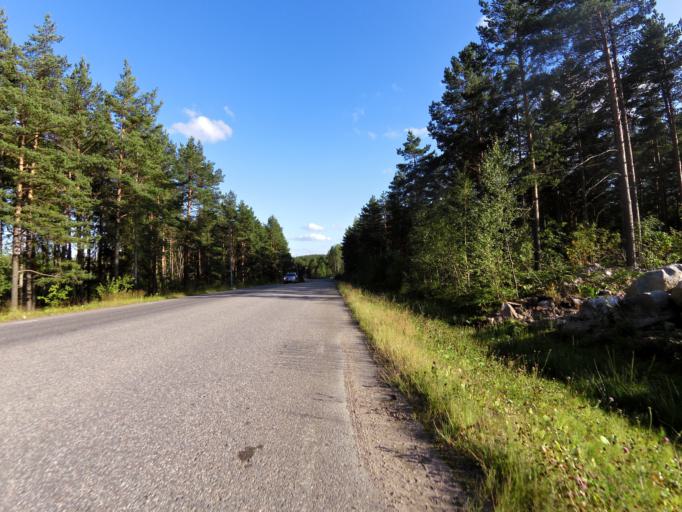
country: SE
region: Gaevleborg
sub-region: Gavle Kommun
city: Gavle
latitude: 60.6483
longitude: 17.1259
